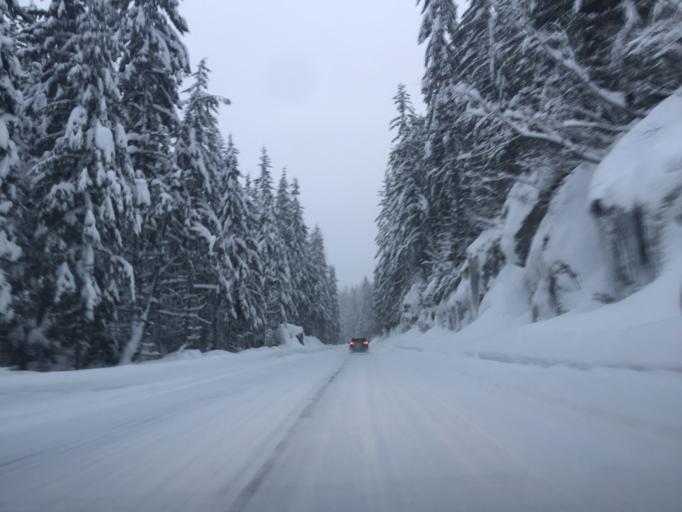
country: US
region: Washington
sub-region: Chelan County
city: Leavenworth
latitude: 47.7801
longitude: -121.0255
